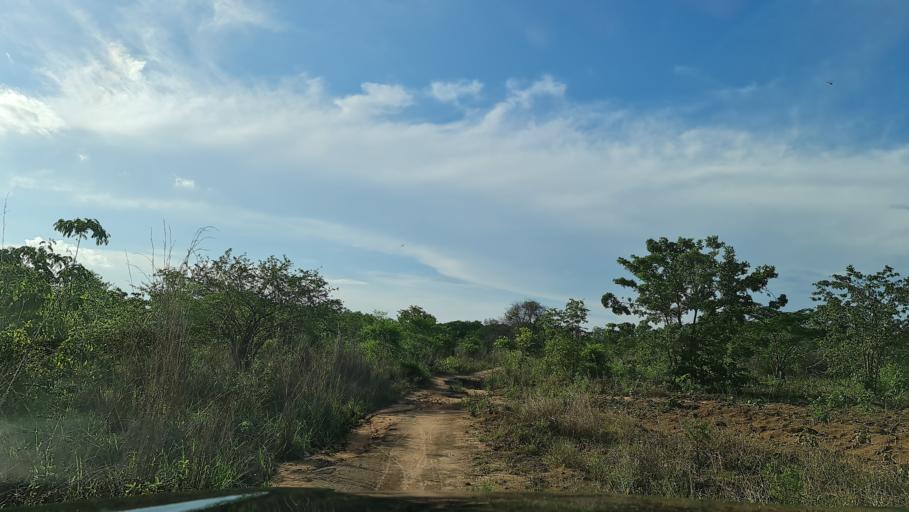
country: MZ
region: Zambezia
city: Quelimane
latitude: -17.1927
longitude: 37.4144
